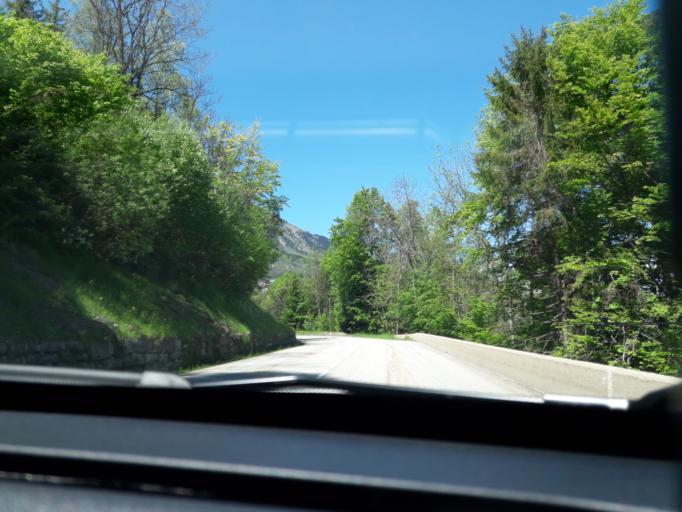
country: FR
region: Rhone-Alpes
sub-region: Departement de la Savoie
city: Saint-Martin-de-Belleville
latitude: 45.4210
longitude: 6.4861
